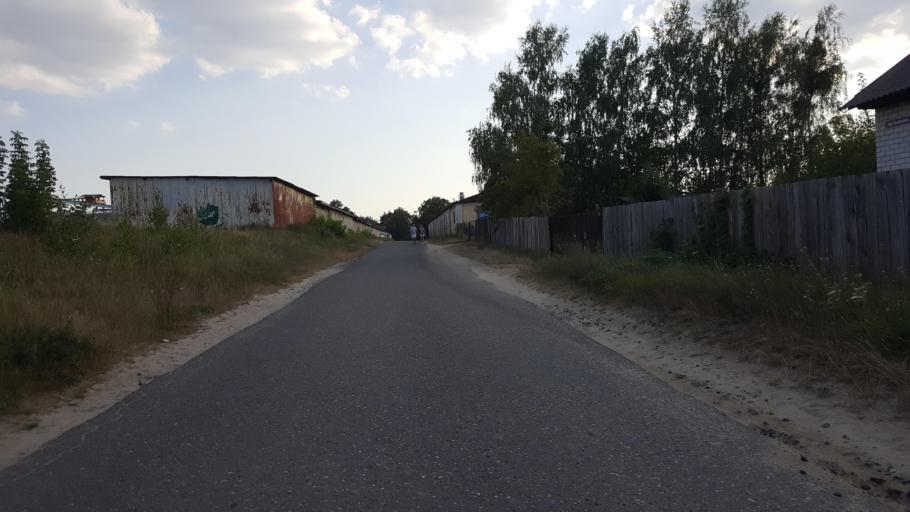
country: BY
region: Brest
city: Kamyanyets
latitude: 52.4045
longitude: 23.8355
